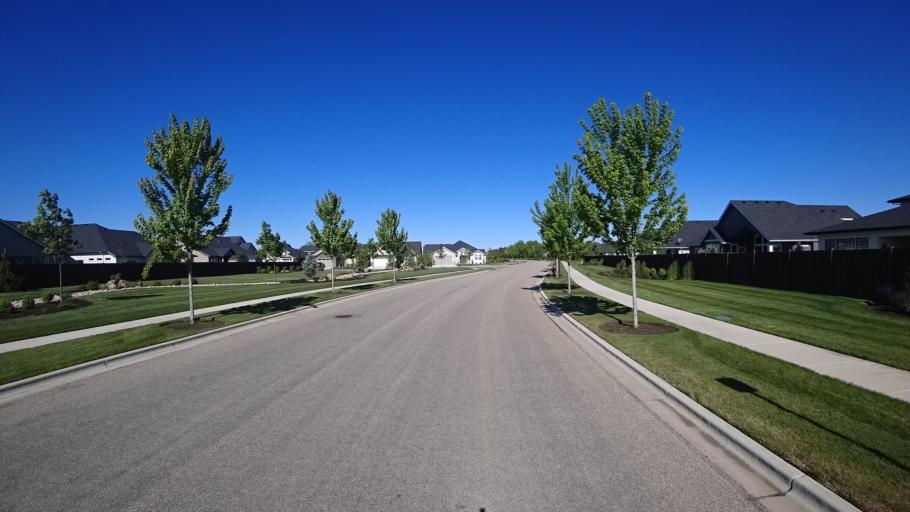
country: US
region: Idaho
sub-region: Ada County
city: Star
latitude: 43.6576
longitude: -116.4494
